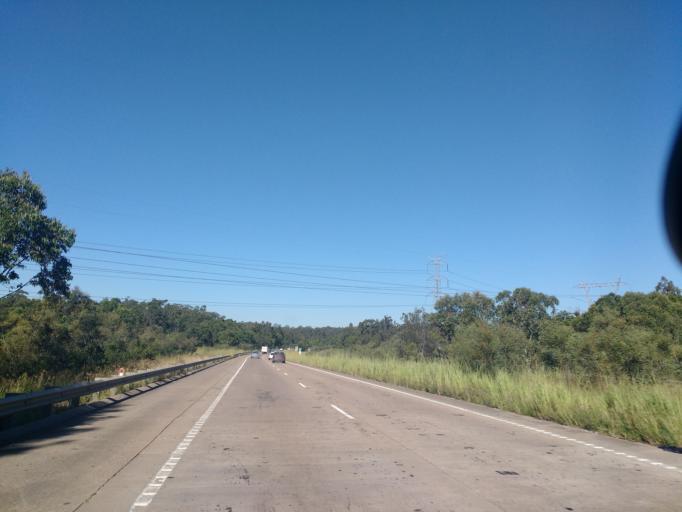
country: AU
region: New South Wales
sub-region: Lake Macquarie Shire
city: Holmesville
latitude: -32.9275
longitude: 151.5507
